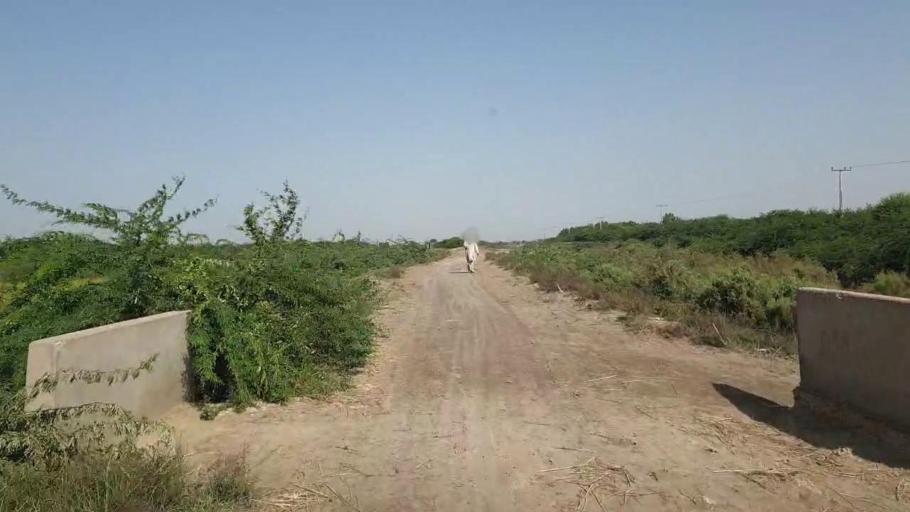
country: PK
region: Sindh
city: Tando Bago
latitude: 24.6978
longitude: 69.0703
